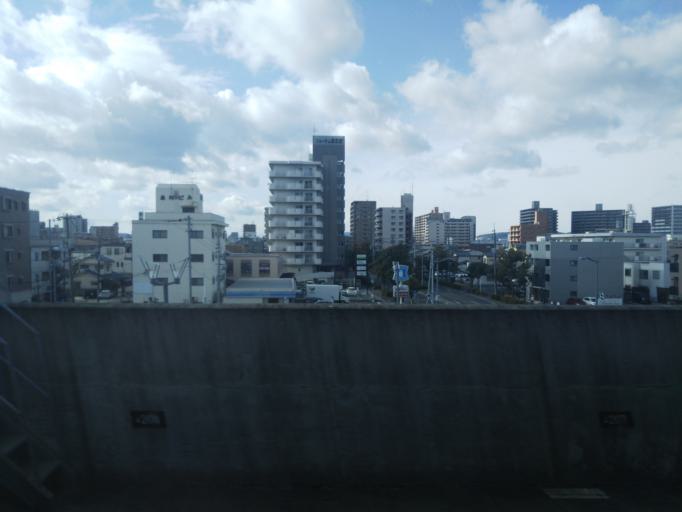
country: JP
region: Okayama
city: Okayama-shi
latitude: 34.6407
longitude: 133.9090
